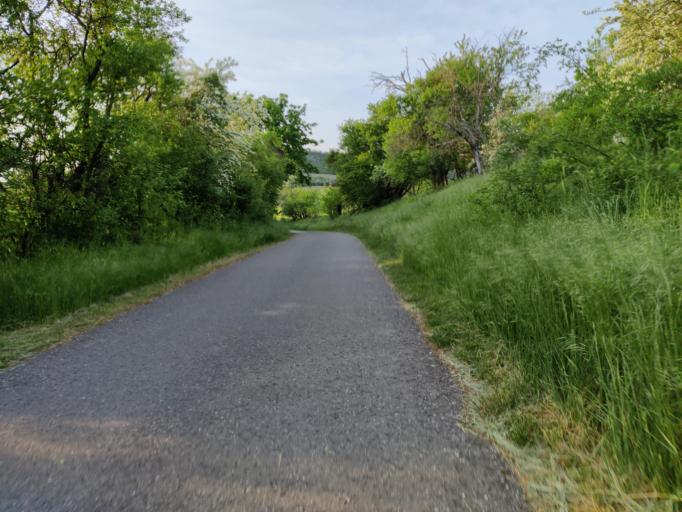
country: DE
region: Saxony-Anhalt
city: Balgstadt
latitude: 51.2201
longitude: 11.7096
